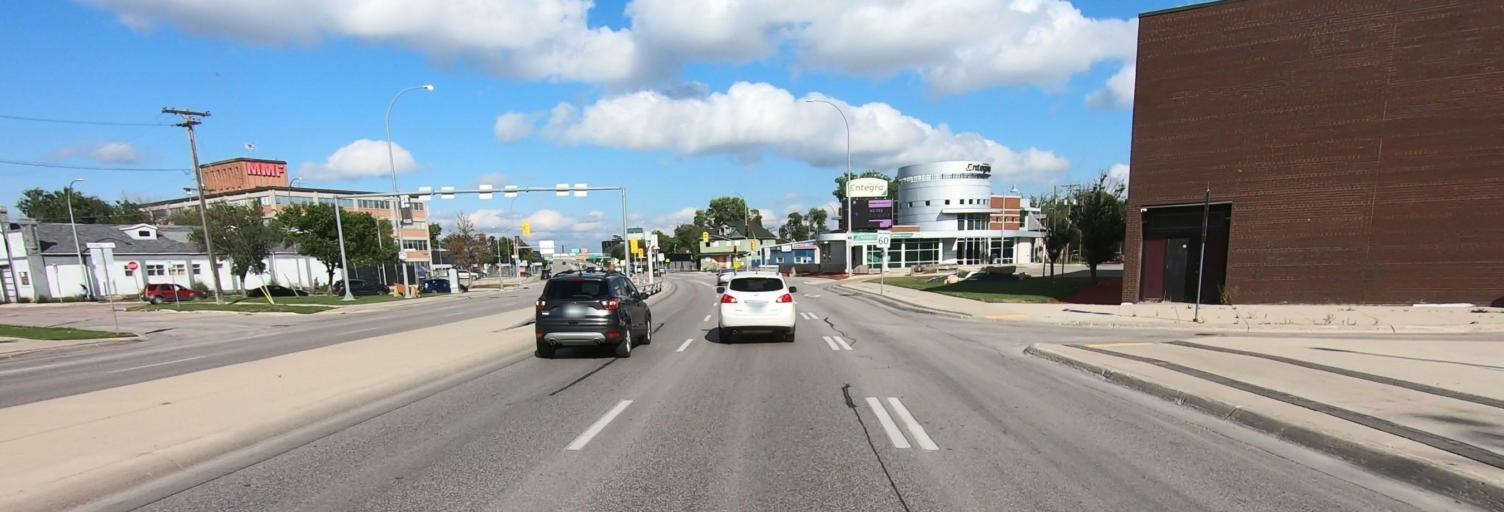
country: CA
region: Manitoba
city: Winnipeg
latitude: 49.9016
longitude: -97.1350
